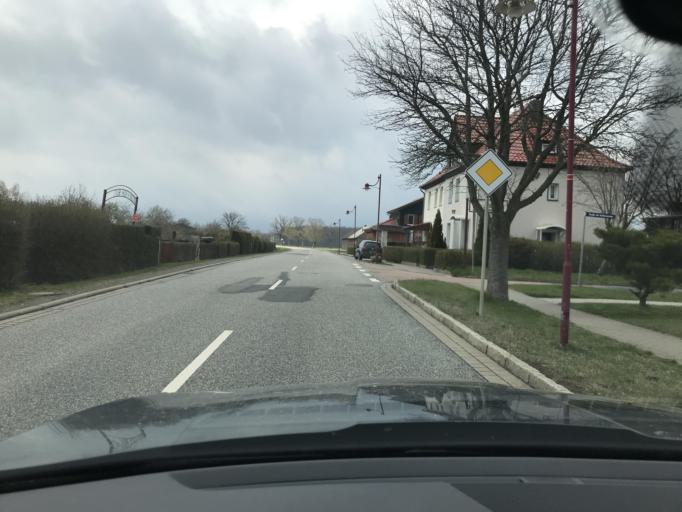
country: DE
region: Saxony-Anhalt
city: Harzgerode
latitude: 51.6495
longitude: 11.1397
